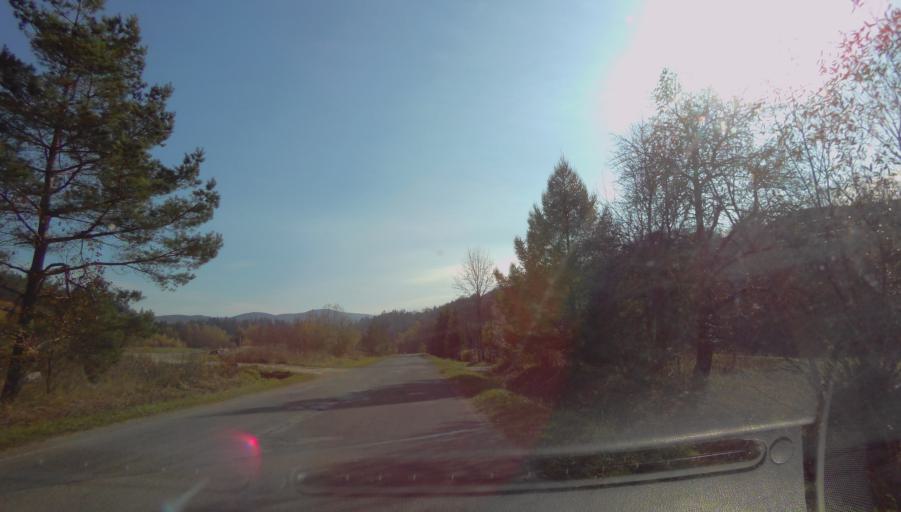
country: PL
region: Subcarpathian Voivodeship
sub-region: Powiat leski
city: Cisna
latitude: 49.2090
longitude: 22.2737
